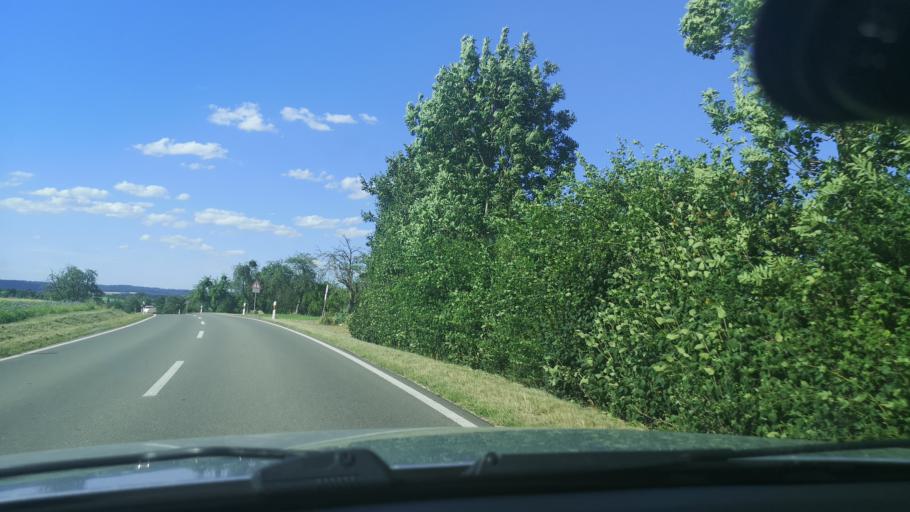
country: DE
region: Baden-Wuerttemberg
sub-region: Regierungsbezirk Stuttgart
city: Zell unter Aichelberg
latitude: 48.6565
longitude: 9.5697
